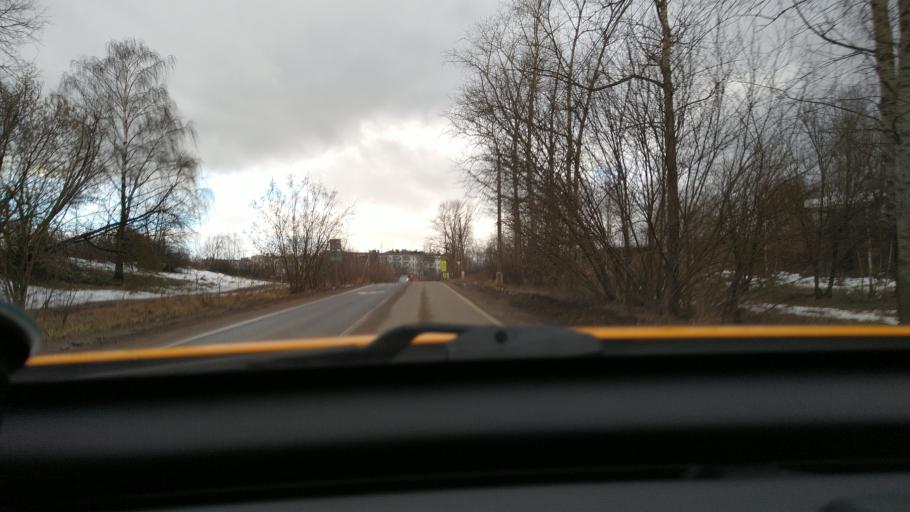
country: RU
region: Moskovskaya
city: Petrovo-Dal'neye
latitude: 55.7656
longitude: 37.2241
